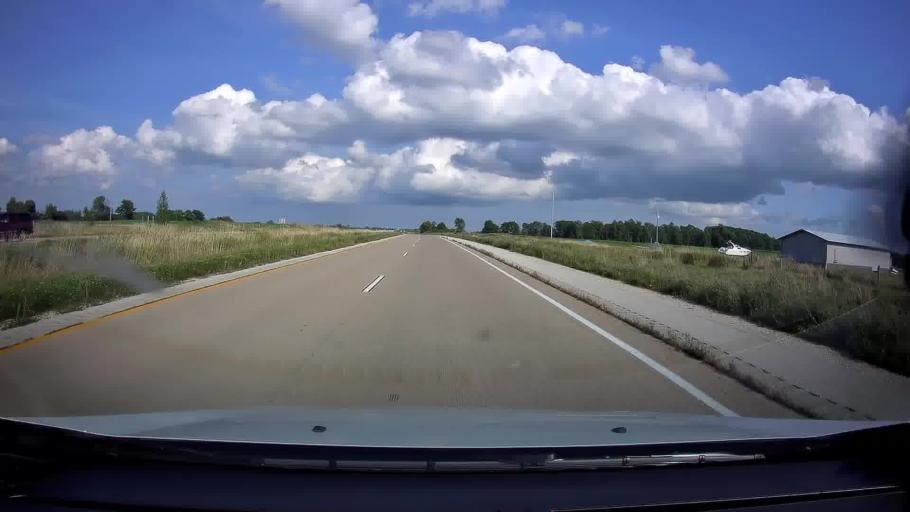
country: US
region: Wisconsin
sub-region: Kewaunee County
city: Luxemburg
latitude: 44.7164
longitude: -87.6626
